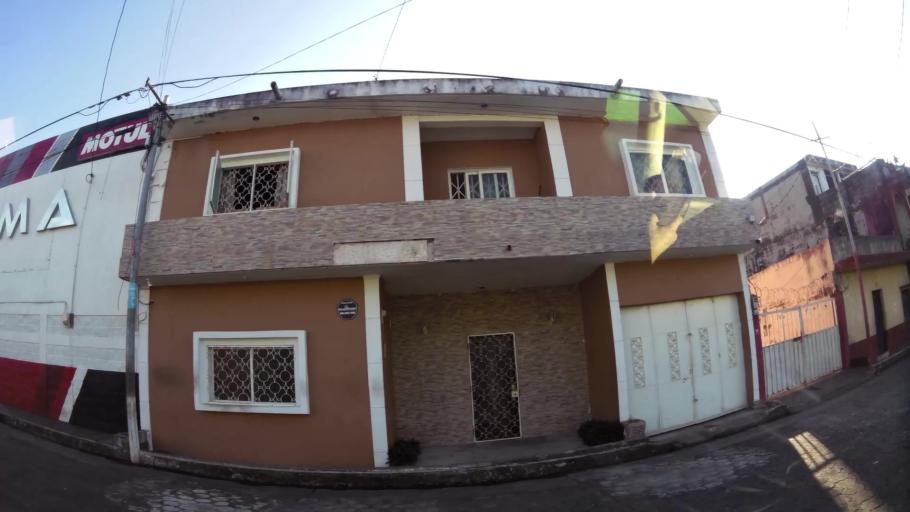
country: GT
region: Suchitepeque
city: Mazatenango
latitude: 14.5293
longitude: -91.5086
